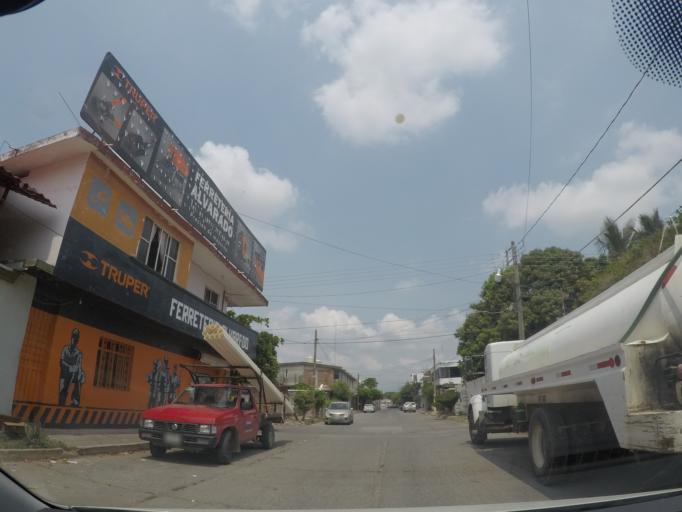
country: MX
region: Oaxaca
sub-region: El Espinal
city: El Espinal
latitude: 16.4864
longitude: -95.0418
